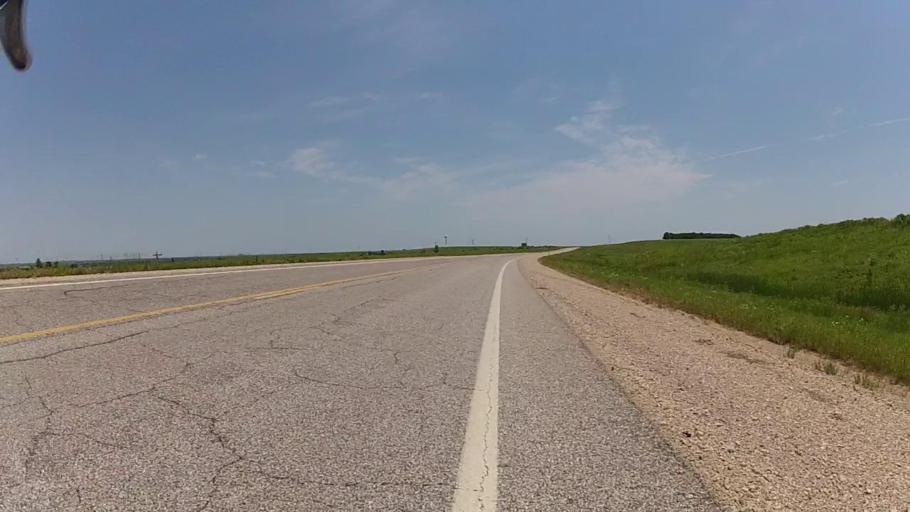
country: US
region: Kansas
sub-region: Chautauqua County
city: Sedan
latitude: 37.1125
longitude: -96.2597
